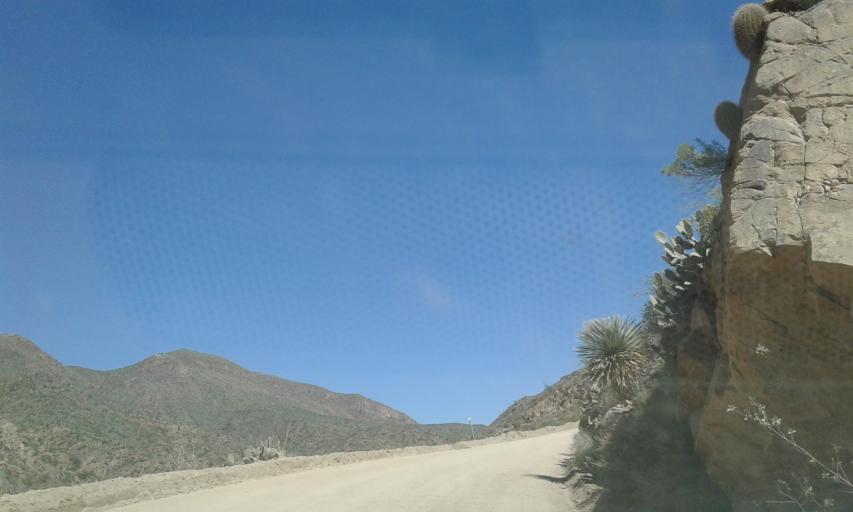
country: US
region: Arizona
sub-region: Gila County
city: Tonto Basin
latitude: 33.6501
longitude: -111.1890
